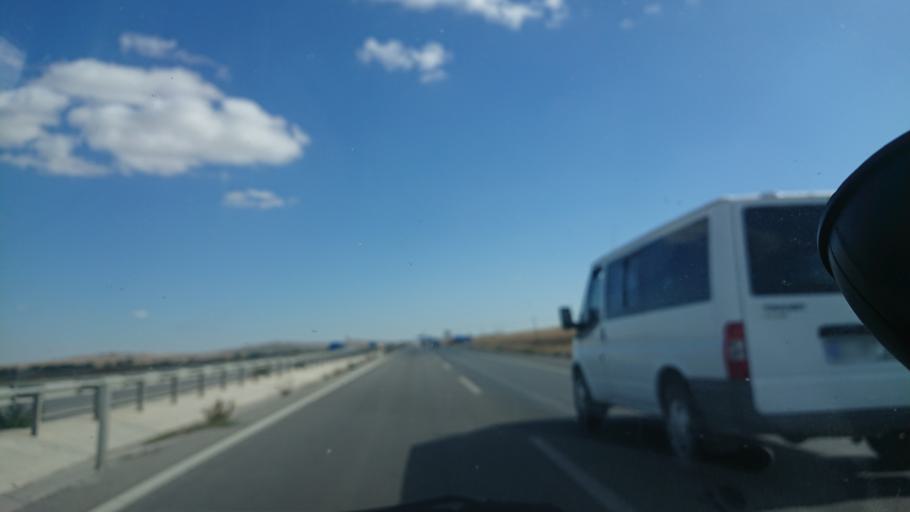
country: TR
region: Eskisehir
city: Mahmudiye
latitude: 39.5258
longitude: 30.9544
